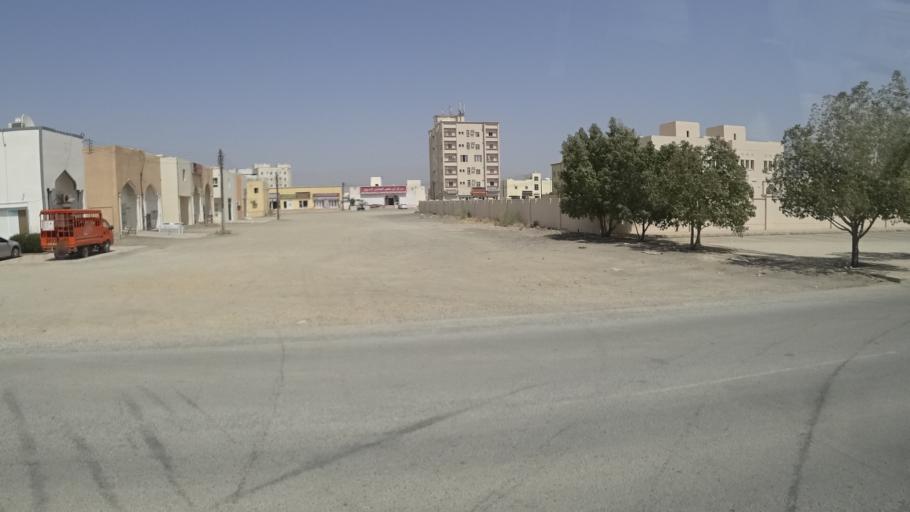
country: OM
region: Muhafazat ad Dakhiliyah
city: Bahla'
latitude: 22.9978
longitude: 57.3178
